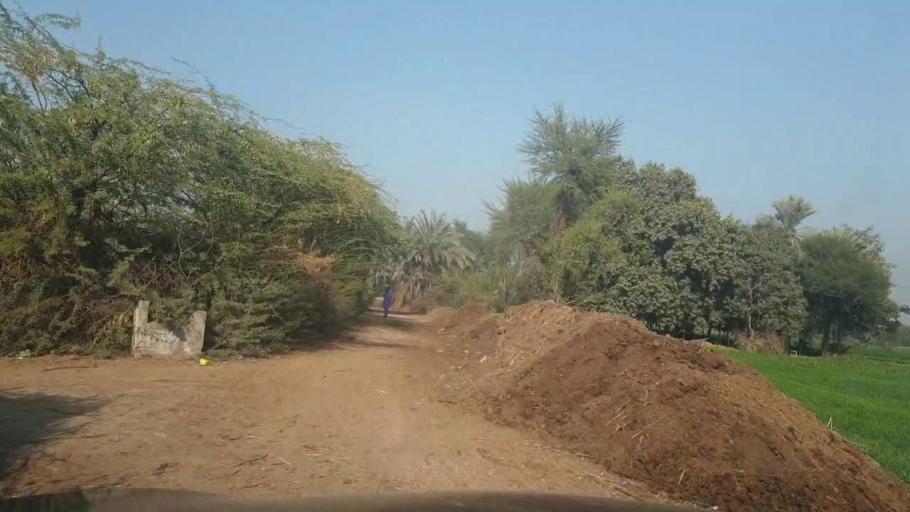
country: PK
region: Sindh
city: Ubauro
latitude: 28.0978
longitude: 69.8422
